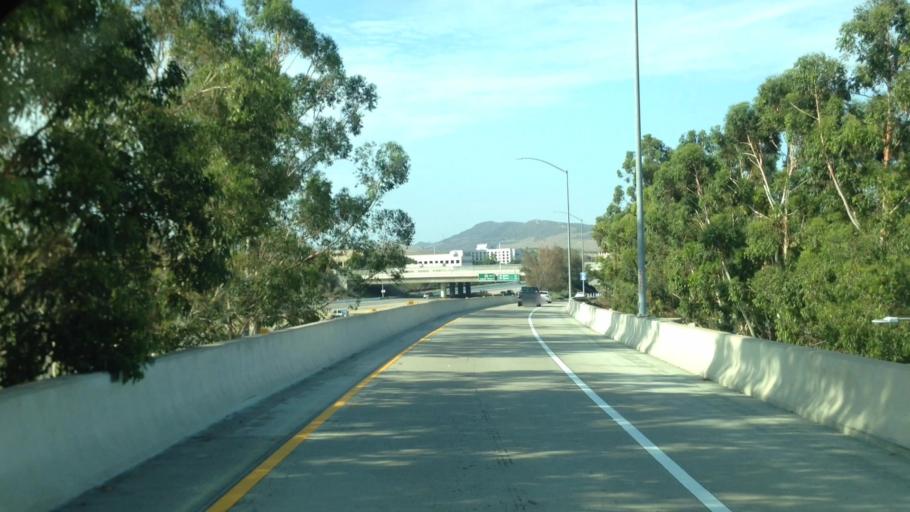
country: US
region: California
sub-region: Orange County
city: Laguna Woods
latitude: 33.6657
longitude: -117.7538
